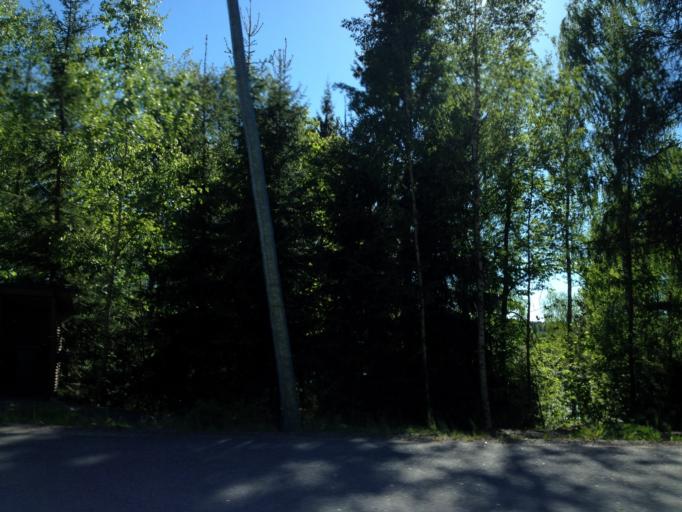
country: FI
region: Uusimaa
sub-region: Helsinki
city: Espoo
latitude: 60.2910
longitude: 24.5623
